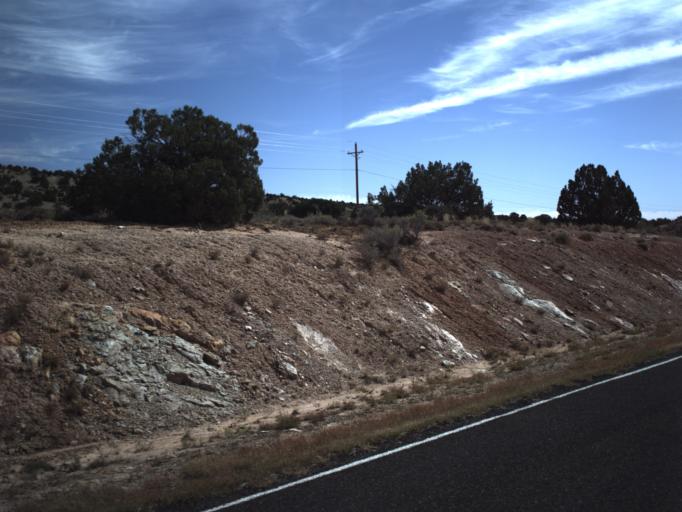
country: US
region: Utah
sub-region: Wayne County
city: Loa
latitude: 37.7474
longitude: -111.5638
